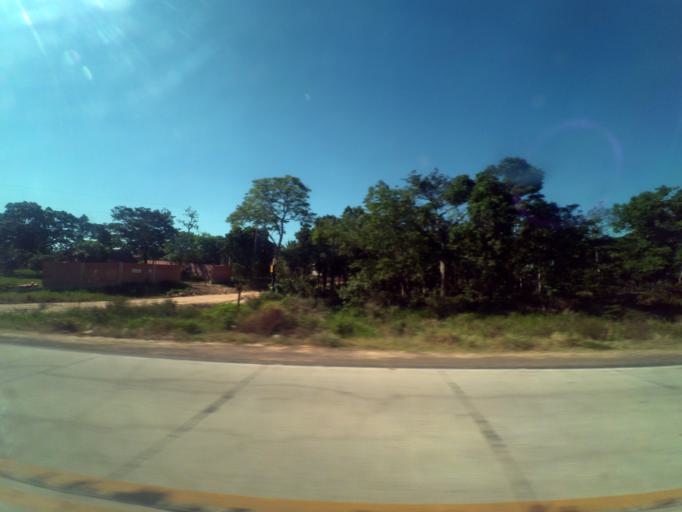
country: BO
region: Santa Cruz
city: Santa Cruz de la Sierra
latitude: -17.7747
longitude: -63.2458
